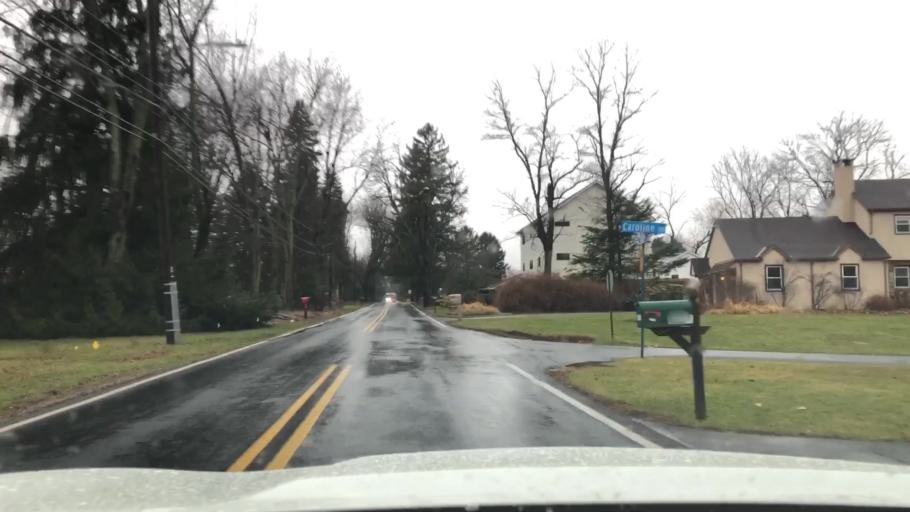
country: US
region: Pennsylvania
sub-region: Lehigh County
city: Dorneyville
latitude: 40.5618
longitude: -75.5262
